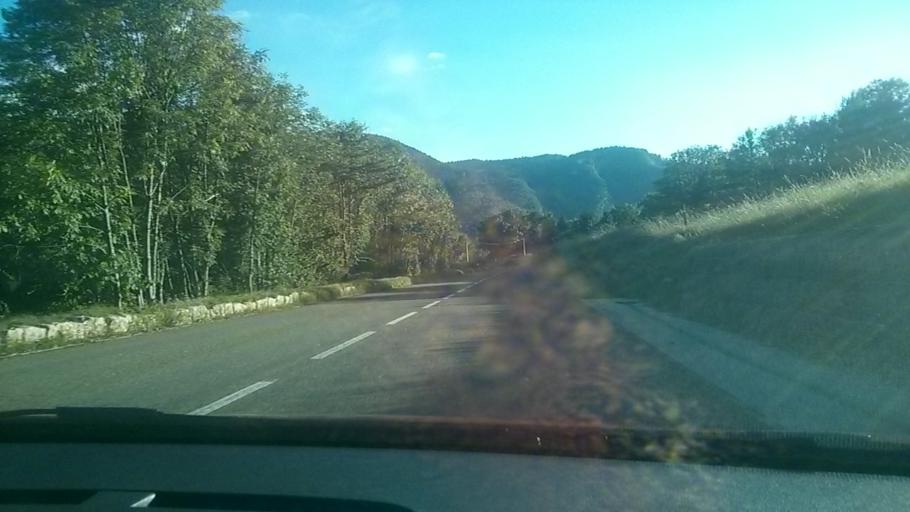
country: FR
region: Franche-Comte
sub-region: Departement du Jura
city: Saint-Claude
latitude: 46.3655
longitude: 5.9135
